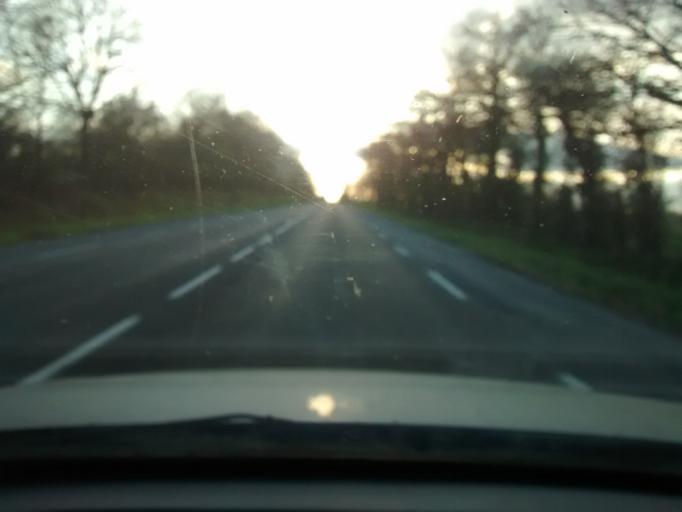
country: FR
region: Pays de la Loire
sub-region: Departement de la Mayenne
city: Vaiges
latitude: 48.0377
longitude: -0.4110
